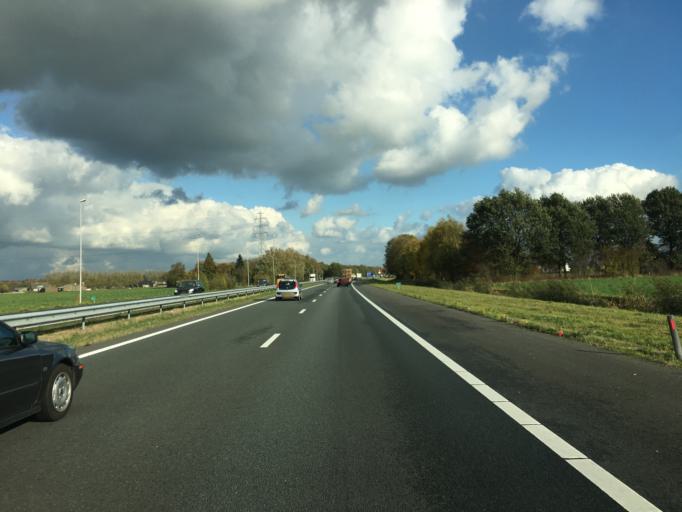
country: NL
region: Gelderland
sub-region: Gemeente Doesburg
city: Doesburg
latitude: 51.9357
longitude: 6.1748
